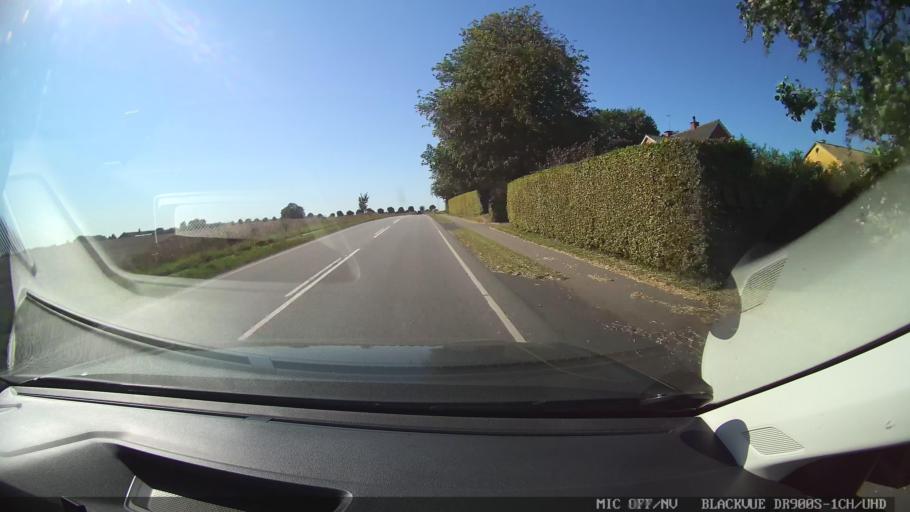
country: DK
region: North Denmark
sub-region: Mariagerfjord Kommune
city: Hobro
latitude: 56.6262
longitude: 9.8355
